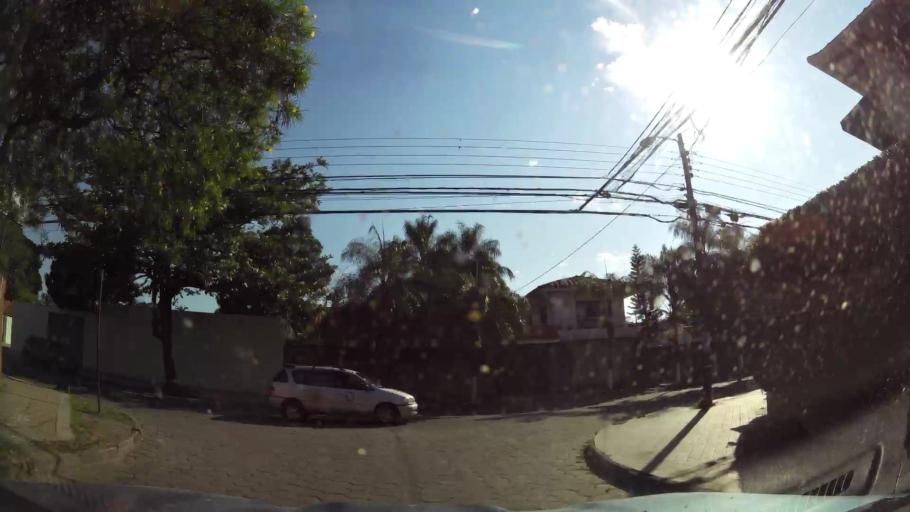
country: BO
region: Santa Cruz
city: Santa Cruz de la Sierra
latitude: -17.7779
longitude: -63.1704
